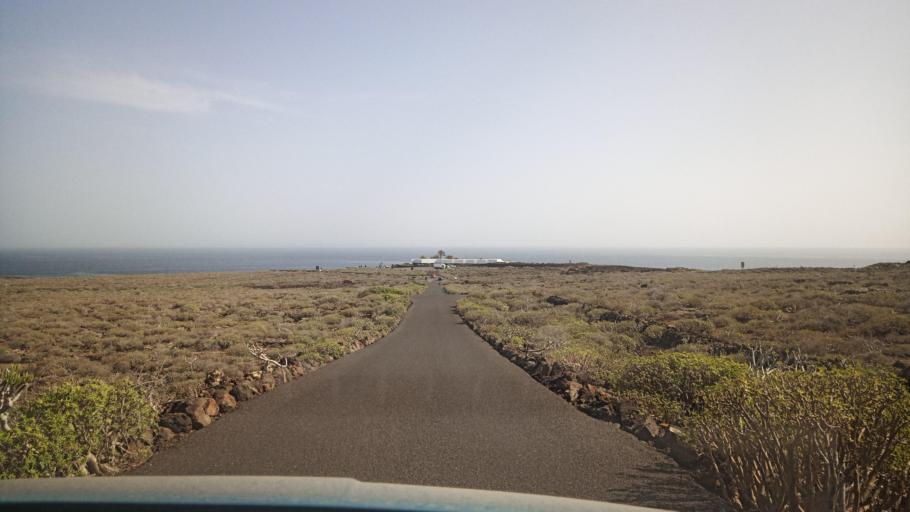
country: ES
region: Canary Islands
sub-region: Provincia de Las Palmas
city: Haria
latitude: 29.1594
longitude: -13.4368
